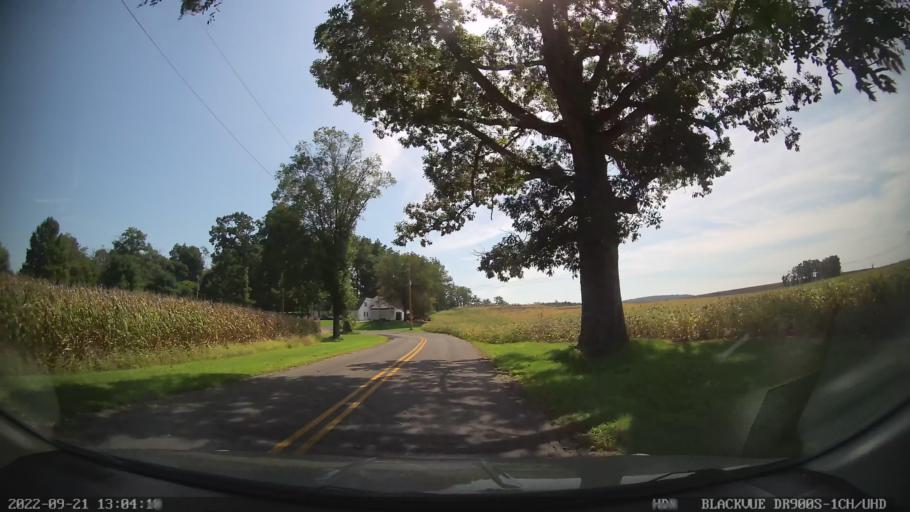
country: US
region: Pennsylvania
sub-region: Berks County
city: Kutztown
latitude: 40.4937
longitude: -75.7486
